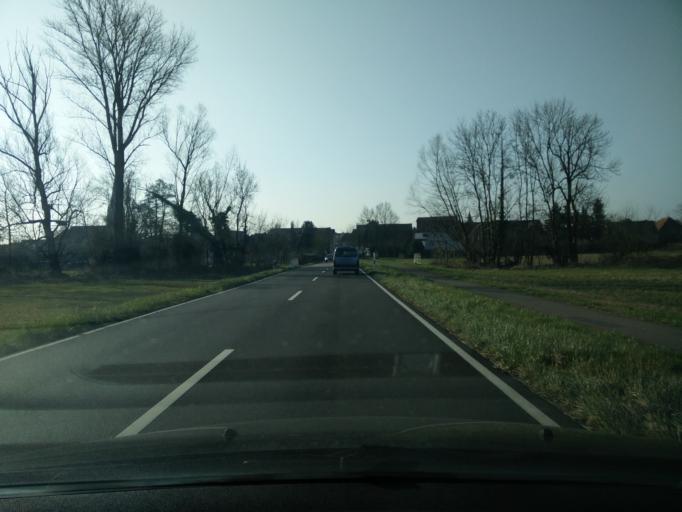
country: DE
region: Rheinland-Pfalz
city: Steinweiler
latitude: 49.1252
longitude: 8.1372
